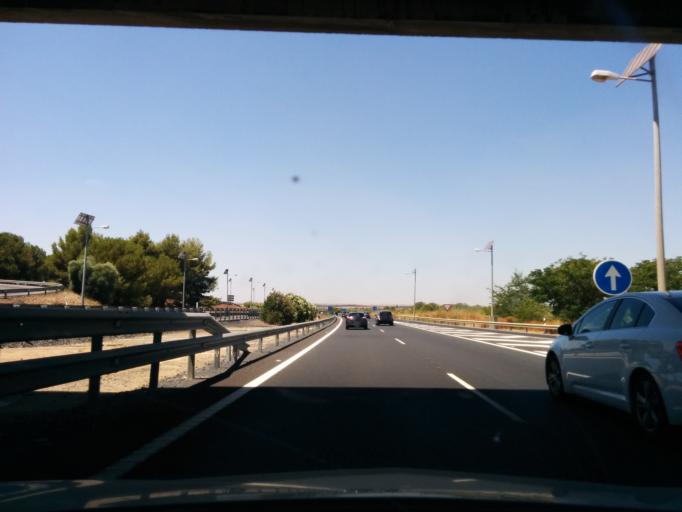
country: ES
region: Andalusia
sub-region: Provincia de Huelva
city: Bonares
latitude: 37.3427
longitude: -6.6762
